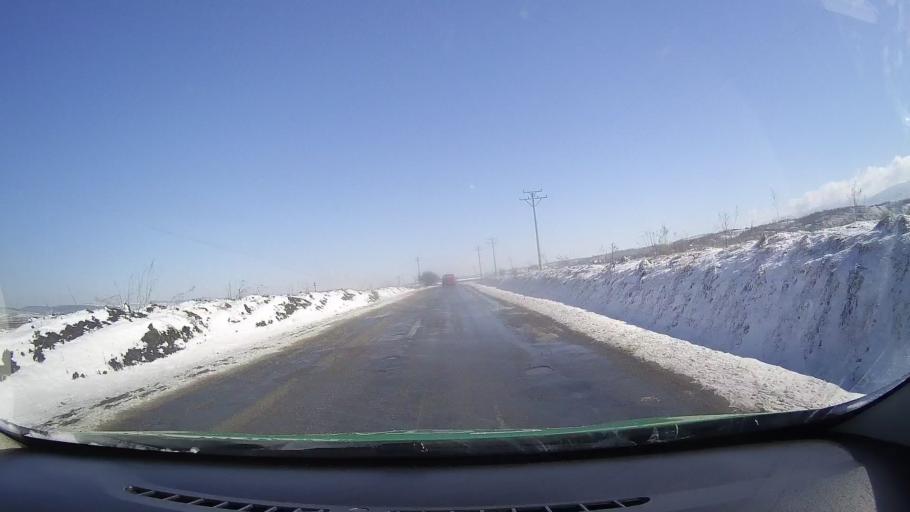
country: RO
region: Sibiu
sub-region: Comuna Racovita
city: Racovita
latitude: 45.6754
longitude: 24.3278
